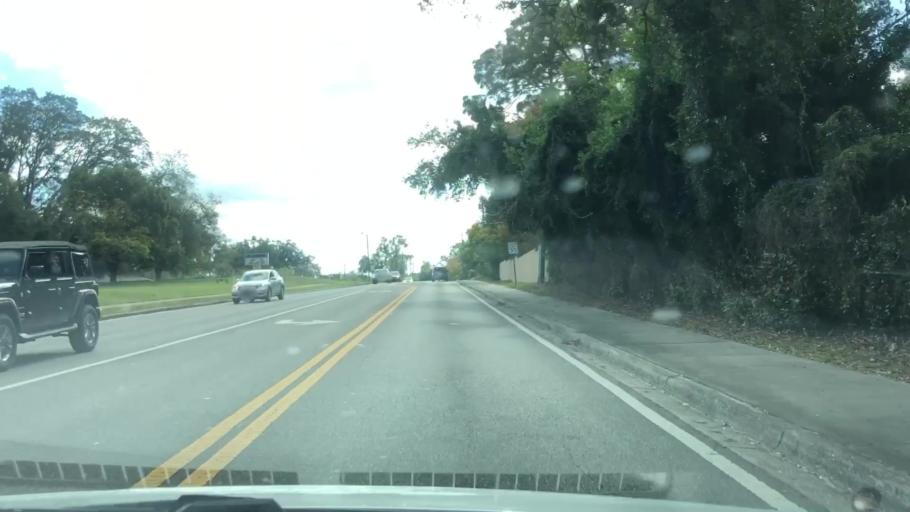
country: US
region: Florida
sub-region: Seminole County
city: Altamonte Springs
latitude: 28.6833
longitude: -81.3738
